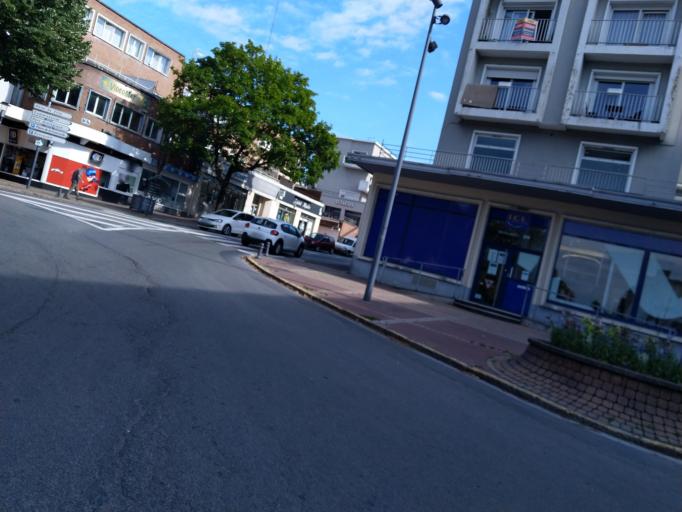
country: FR
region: Nord-Pas-de-Calais
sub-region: Departement du Nord
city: Maubeuge
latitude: 50.2768
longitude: 3.9739
